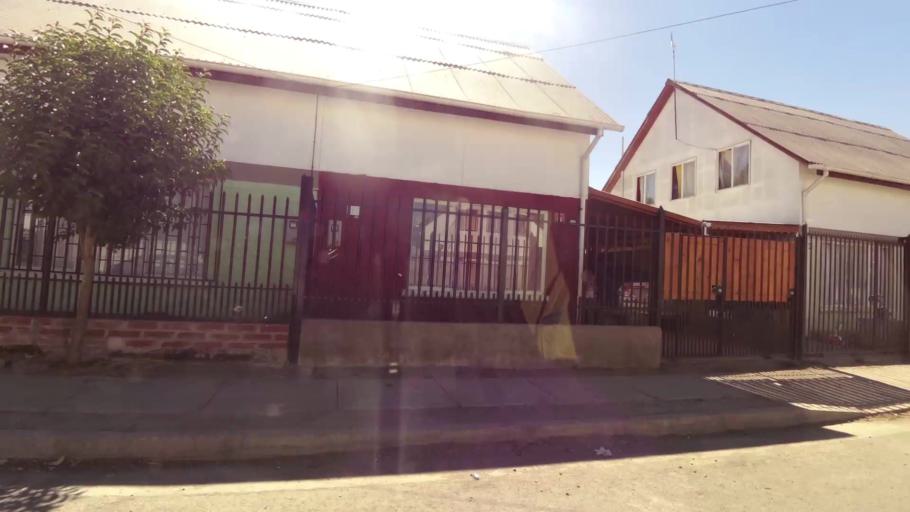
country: CL
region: O'Higgins
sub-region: Provincia de Colchagua
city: Chimbarongo
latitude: -34.5936
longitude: -71.0020
